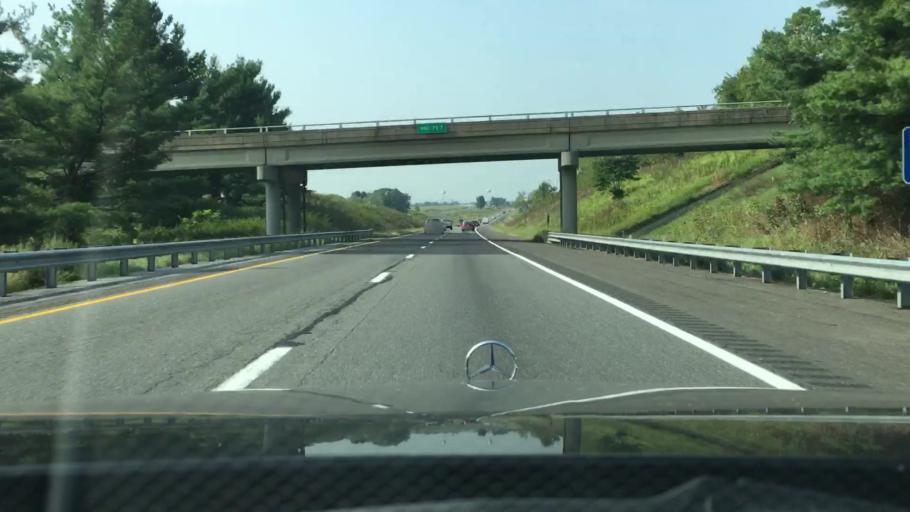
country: US
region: Virginia
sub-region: Shenandoah County
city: Mount Jackson
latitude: 38.7864
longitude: -78.6118
